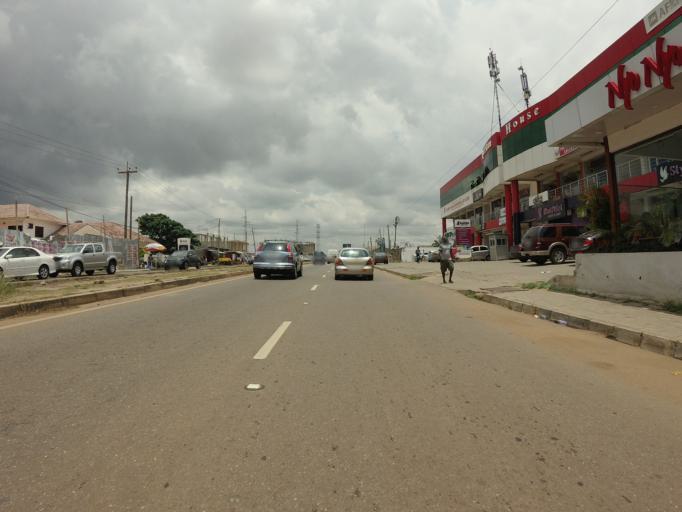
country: GH
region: Greater Accra
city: Medina Estates
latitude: 5.6469
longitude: -0.1496
